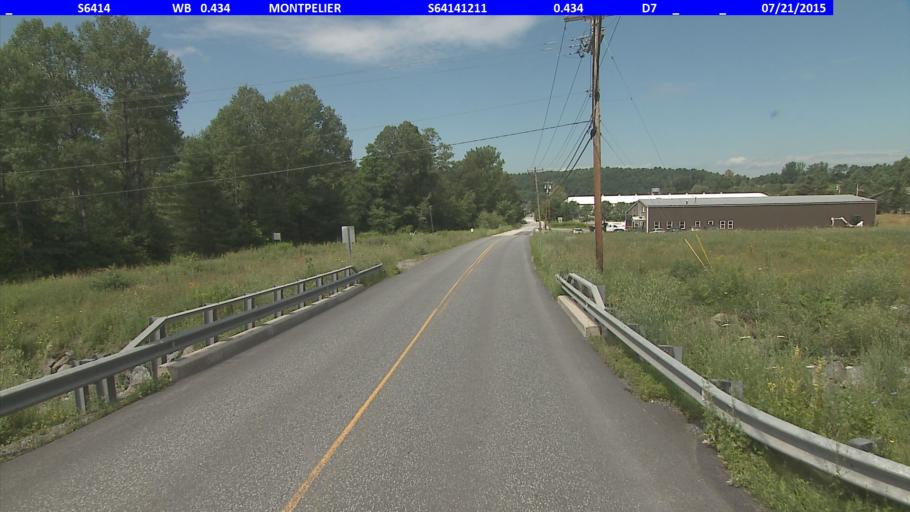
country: US
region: Vermont
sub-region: Washington County
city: Montpelier
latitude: 44.2426
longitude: -72.5363
